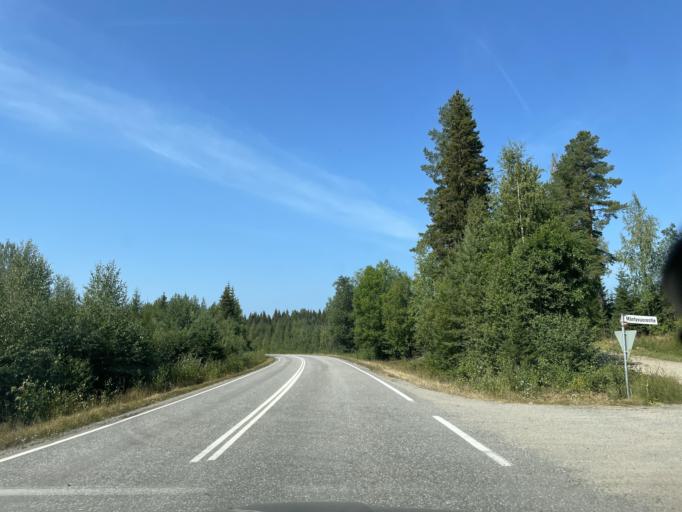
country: FI
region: Central Finland
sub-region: Saarijaervi-Viitasaari
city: Pihtipudas
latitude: 63.3744
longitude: 25.6088
